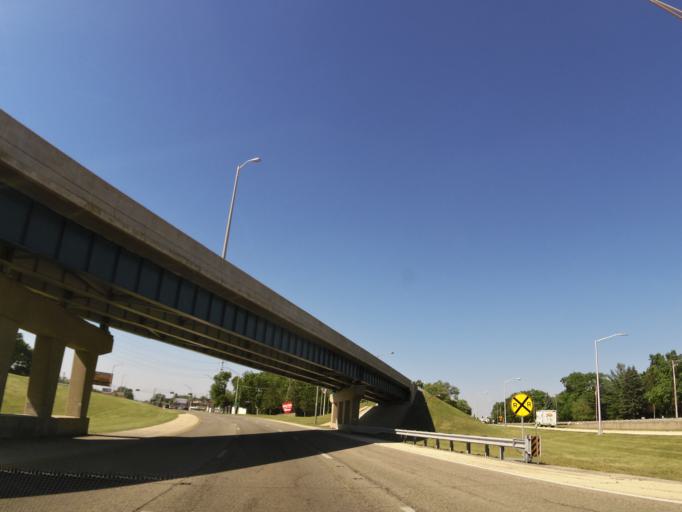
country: US
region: Illinois
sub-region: Winnebago County
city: Loves Park
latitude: 42.2958
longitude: -89.0577
